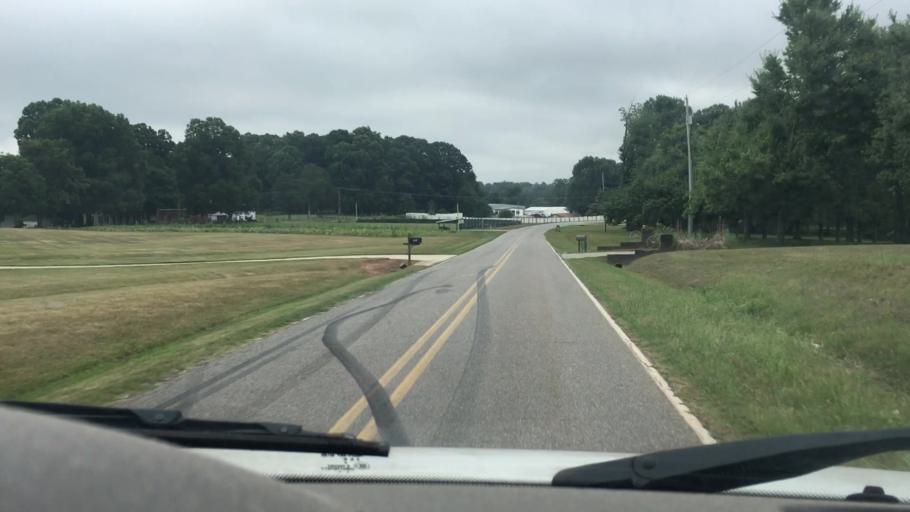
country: US
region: North Carolina
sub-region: Gaston County
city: Davidson
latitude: 35.5310
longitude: -80.8288
